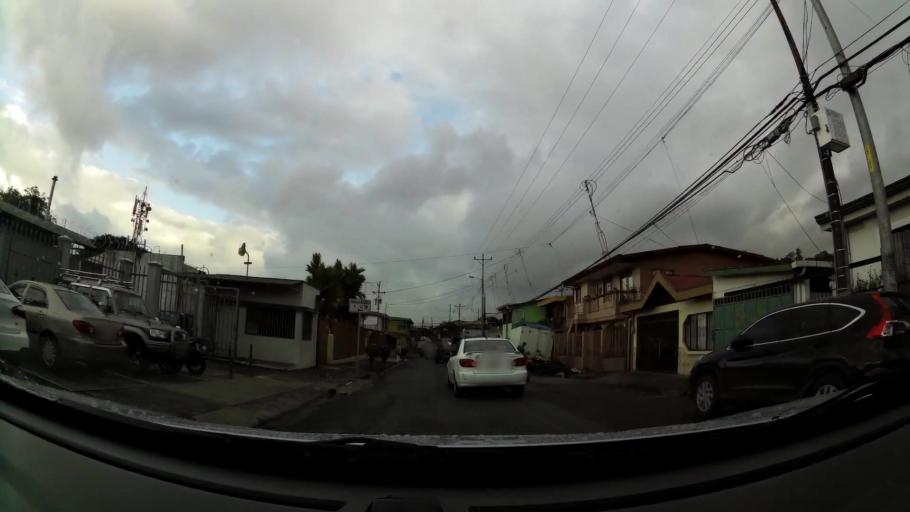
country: CR
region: Cartago
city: Turrialba
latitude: 9.9031
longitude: -83.6848
